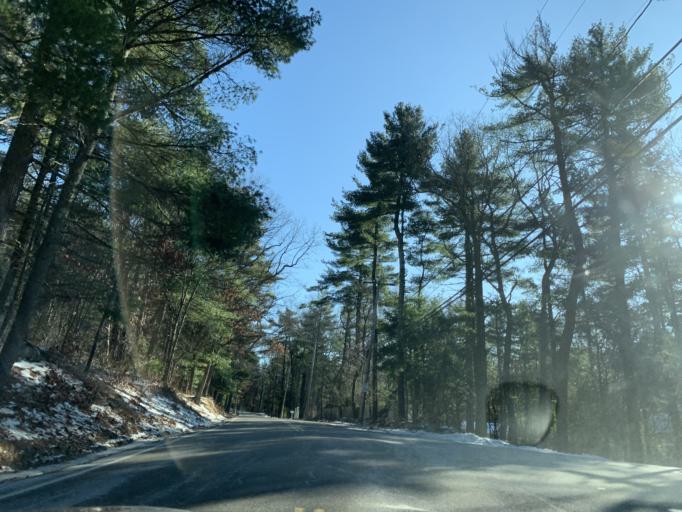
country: US
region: Massachusetts
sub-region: Norfolk County
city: Canton
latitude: 42.1979
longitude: -71.1255
